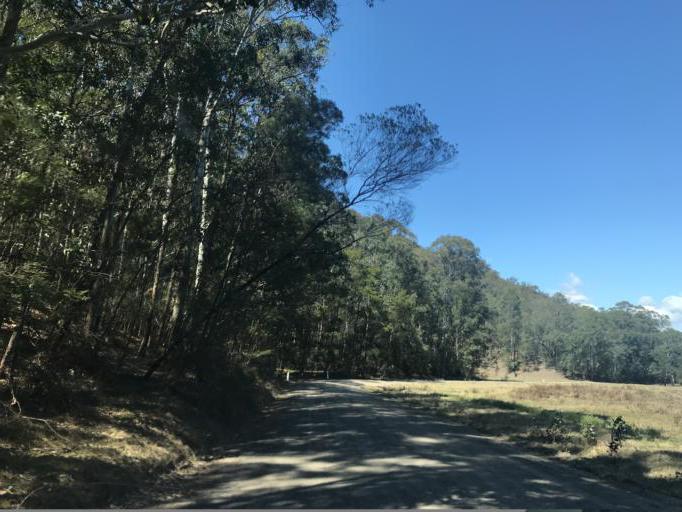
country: AU
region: New South Wales
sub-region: Hornsby Shire
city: Glenorie
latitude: -33.2187
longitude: 150.9794
